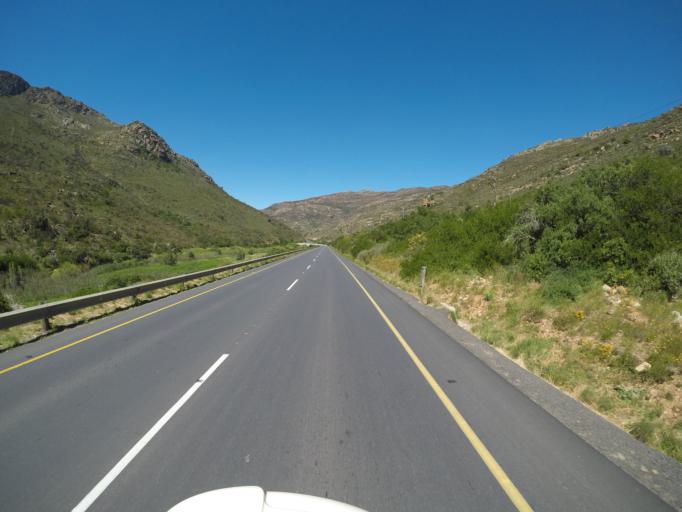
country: ZA
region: Western Cape
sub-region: Cape Winelands District Municipality
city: Ceres
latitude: -33.3094
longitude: 19.0712
